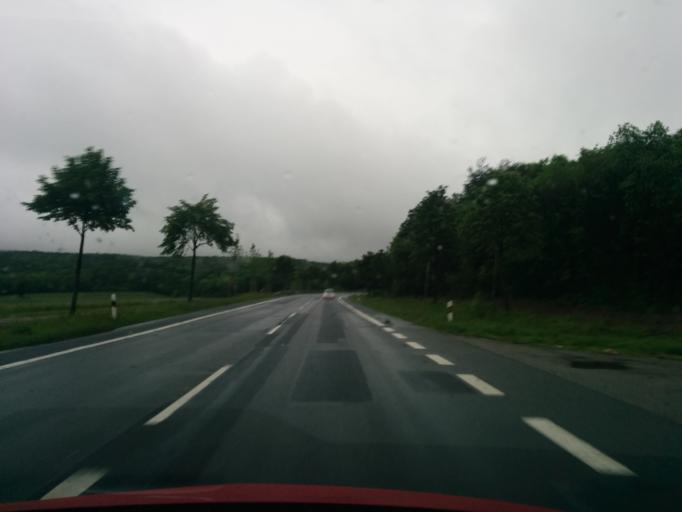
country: DE
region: Lower Saxony
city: Waake
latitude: 51.5595
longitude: 10.0160
